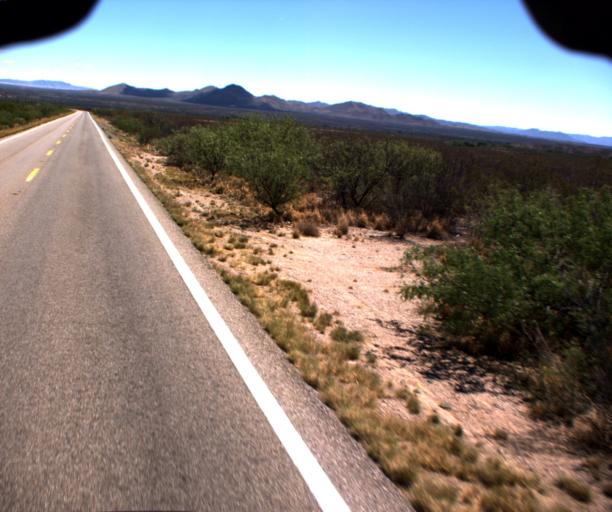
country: US
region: Arizona
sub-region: Cochise County
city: Huachuca City
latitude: 31.7209
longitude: -110.2189
